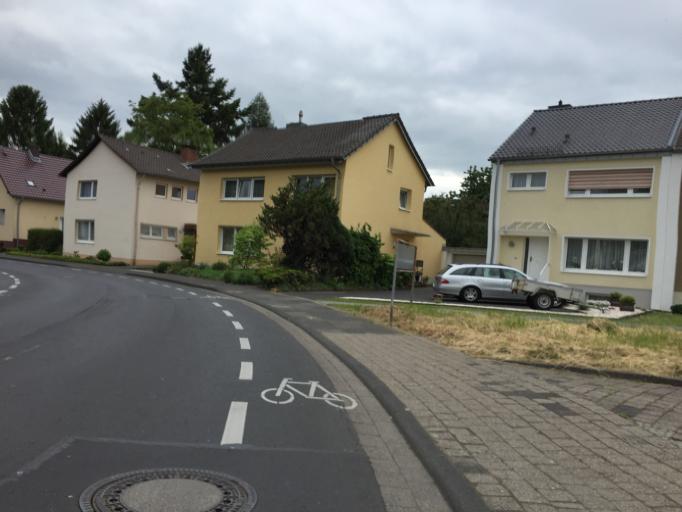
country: DE
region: North Rhine-Westphalia
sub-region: Regierungsbezirk Koln
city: Bonn
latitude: 50.7163
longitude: 7.0712
